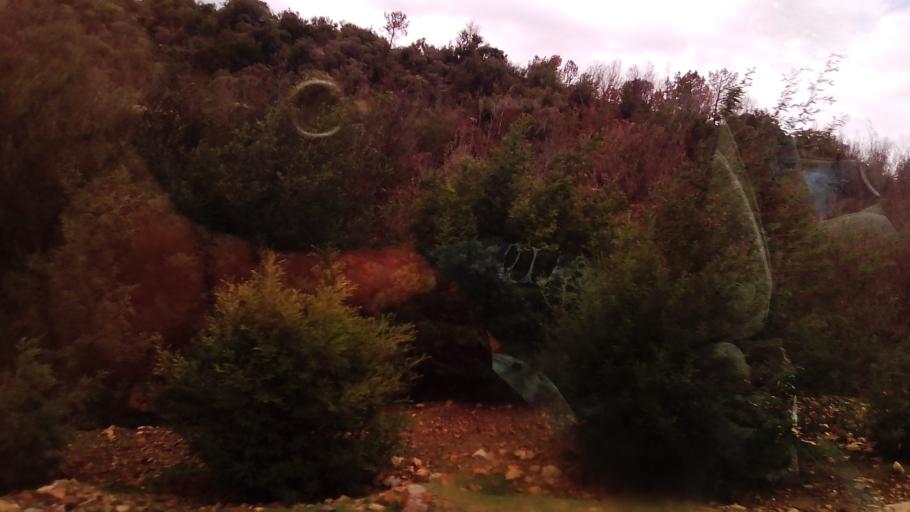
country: LS
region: Berea
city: Teyateyaneng
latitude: -29.3318
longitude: 27.7060
